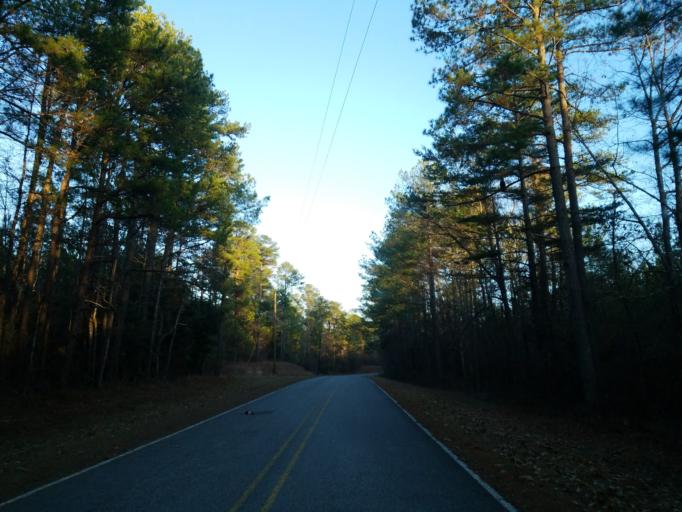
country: US
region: Mississippi
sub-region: Clarke County
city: Stonewall
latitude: 32.2637
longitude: -88.8014
